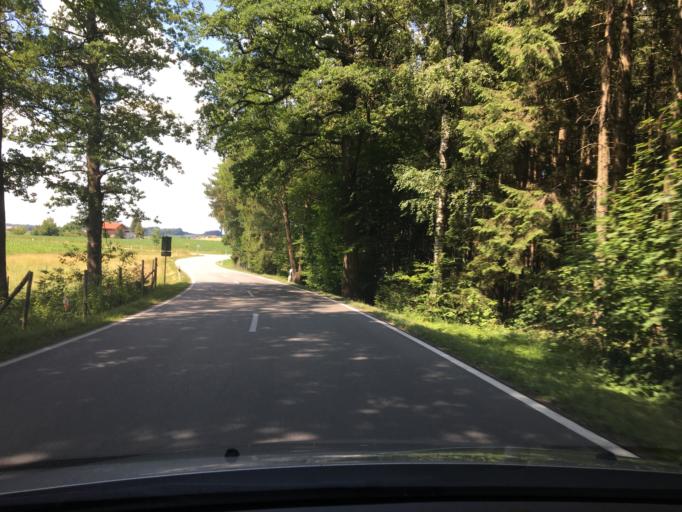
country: DE
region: Bavaria
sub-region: Upper Bavaria
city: Neumarkt-Sankt Veit
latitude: 48.3748
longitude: 12.5070
